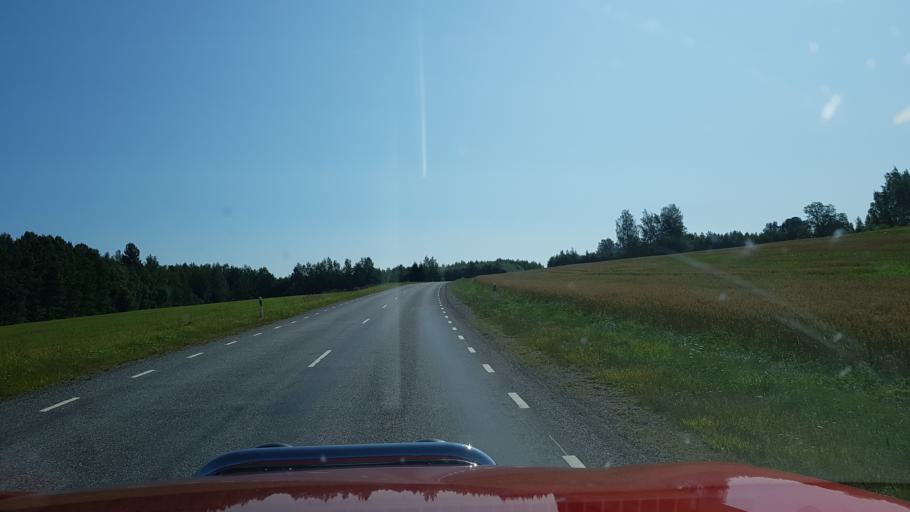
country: EE
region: Vorumaa
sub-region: Voru linn
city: Voru
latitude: 57.9766
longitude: 26.8091
